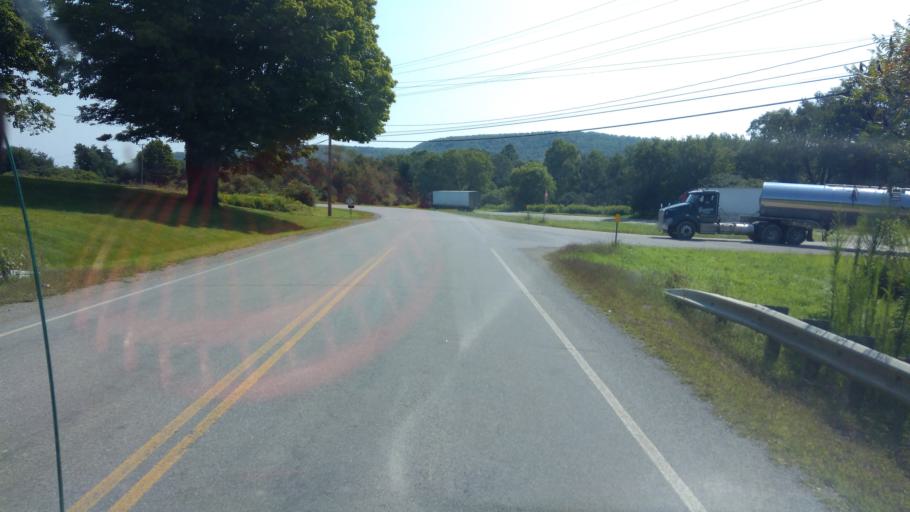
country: US
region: New York
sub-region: Allegany County
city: Friendship
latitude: 42.2150
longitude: -78.1139
